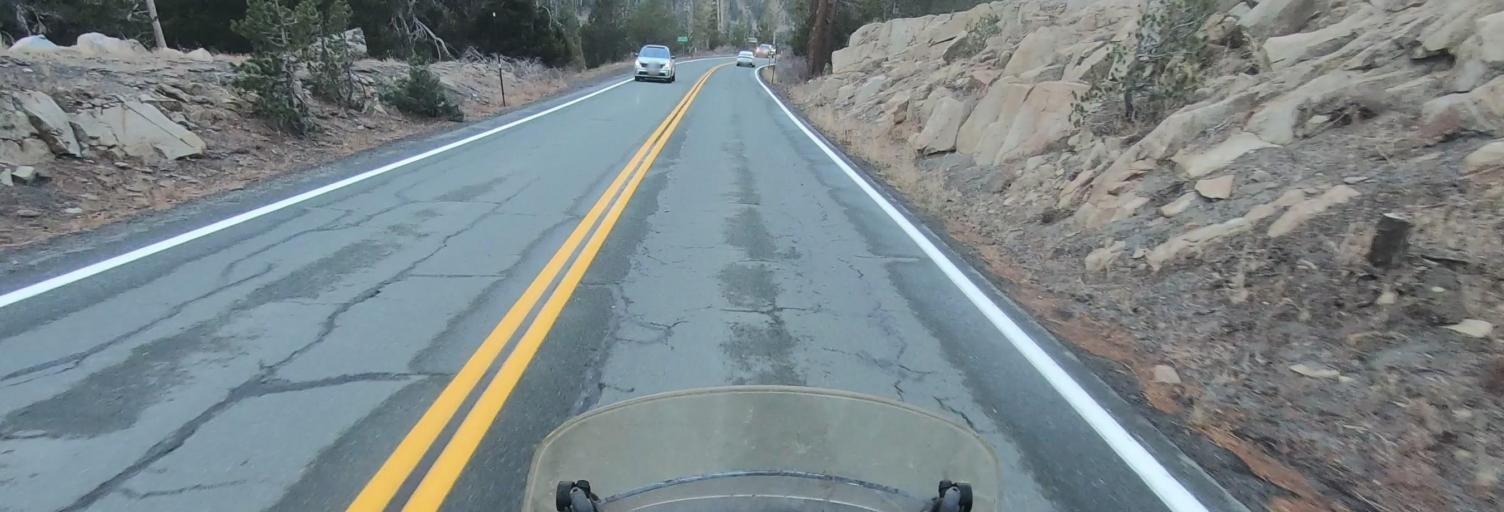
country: US
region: California
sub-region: El Dorado County
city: South Lake Tahoe
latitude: 38.7039
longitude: -120.0532
